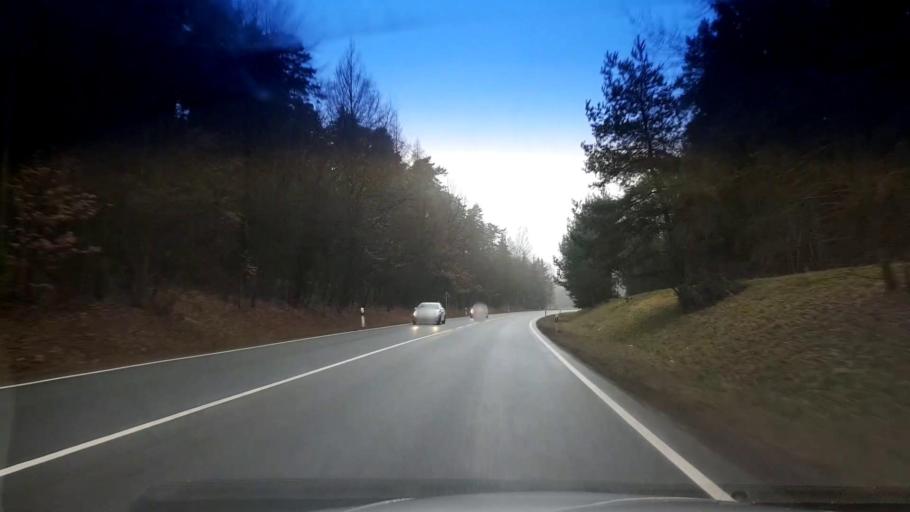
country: DE
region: Bavaria
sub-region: Upper Palatinate
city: Tirschenreuth
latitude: 49.8933
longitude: 12.3106
